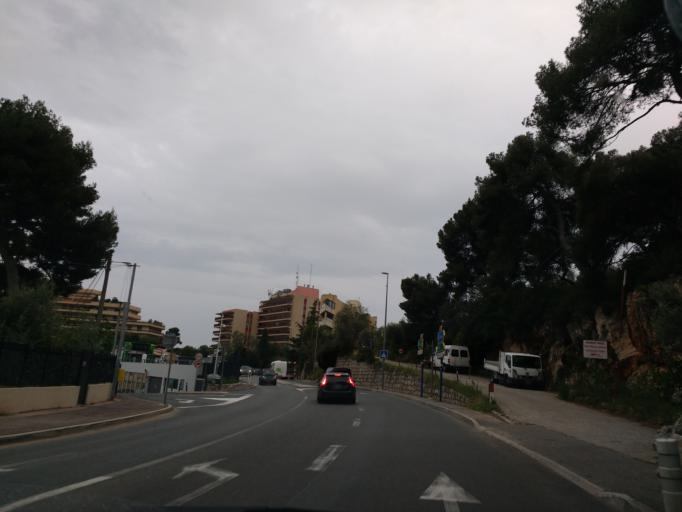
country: MC
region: Commune de Monaco
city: Moneghetti
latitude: 43.7370
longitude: 7.4123
